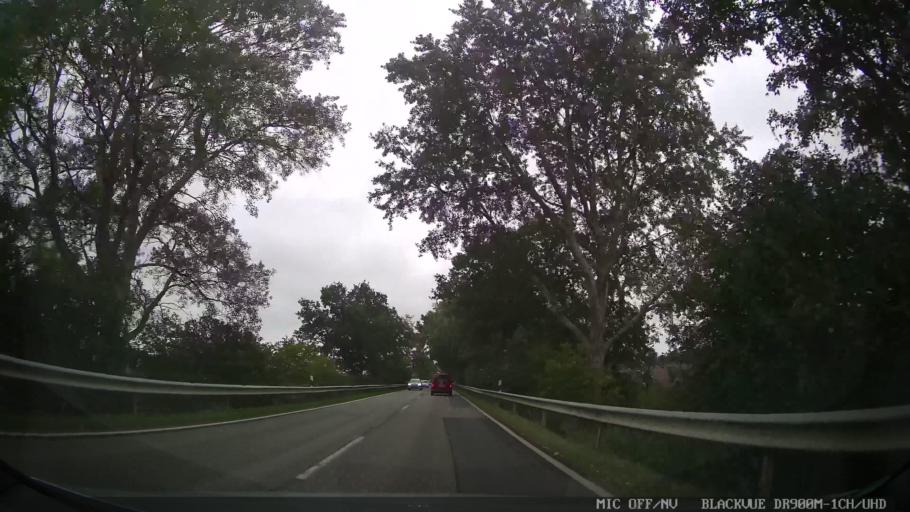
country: DE
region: Schleswig-Holstein
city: Neukirchen
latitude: 54.3258
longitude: 11.0203
